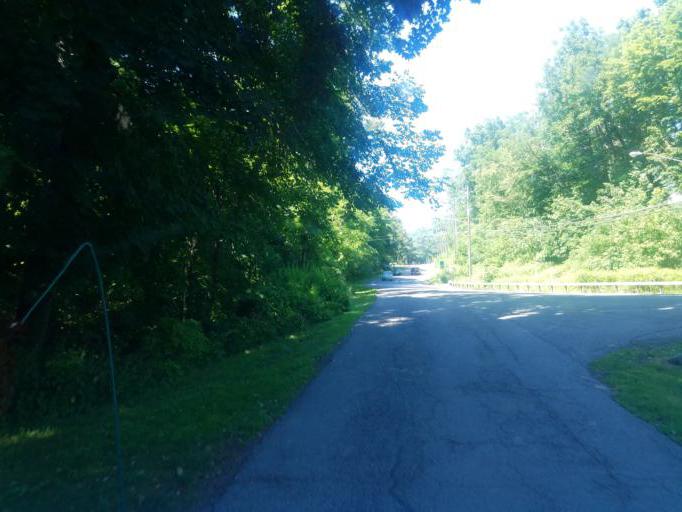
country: US
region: New York
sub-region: Ontario County
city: Geneva
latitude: 42.8503
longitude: -76.9811
